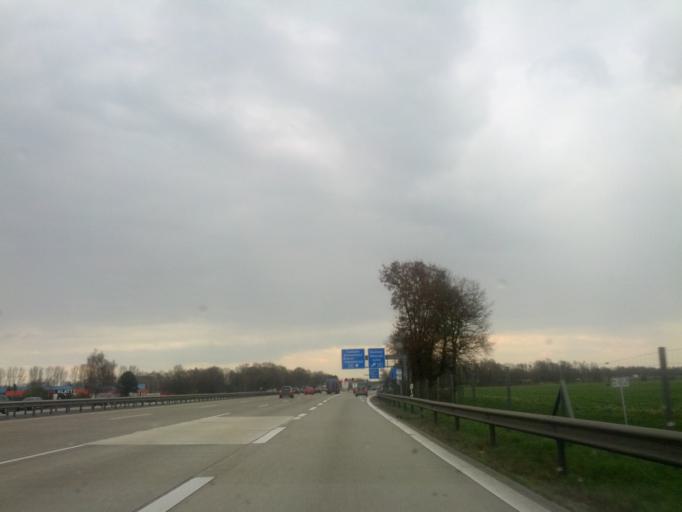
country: DE
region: Lower Saxony
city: Oyten
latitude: 53.0381
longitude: 8.9755
